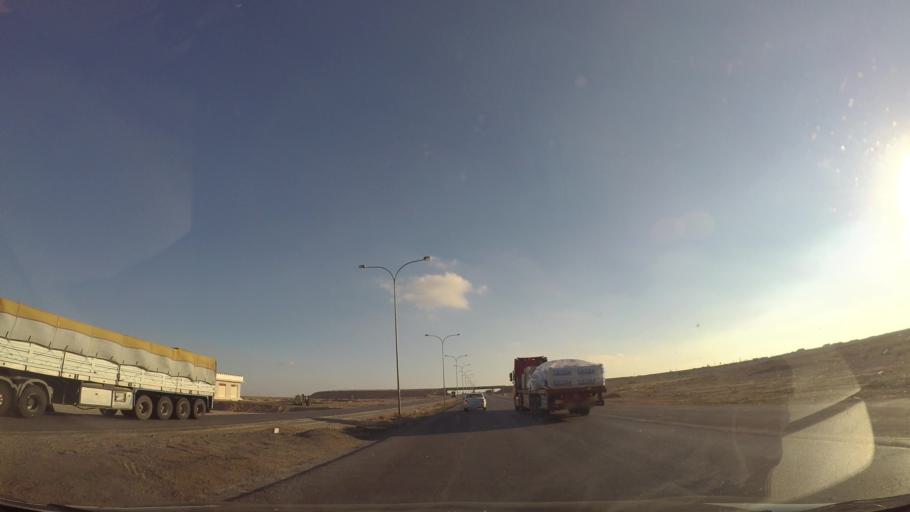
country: JO
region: Tafielah
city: Busayra
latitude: 30.5805
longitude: 35.8002
